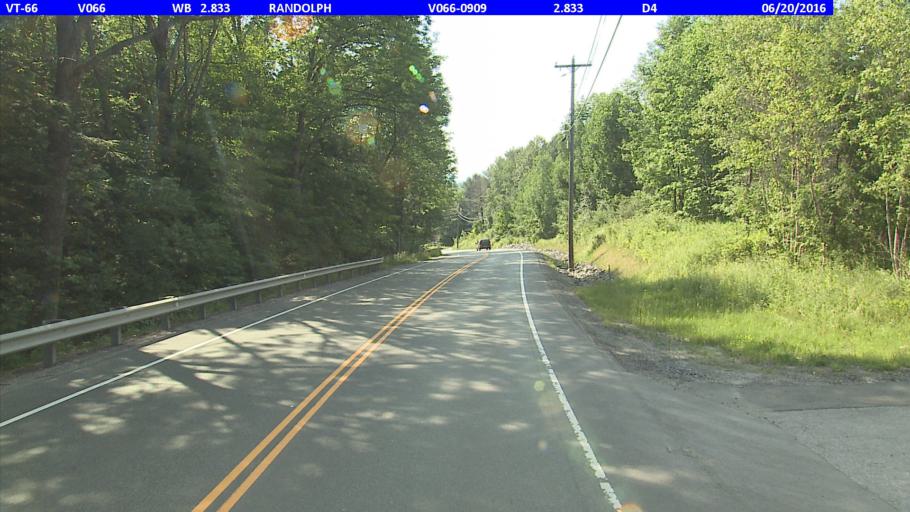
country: US
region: Vermont
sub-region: Orange County
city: Randolph
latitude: 43.9443
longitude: -72.6158
